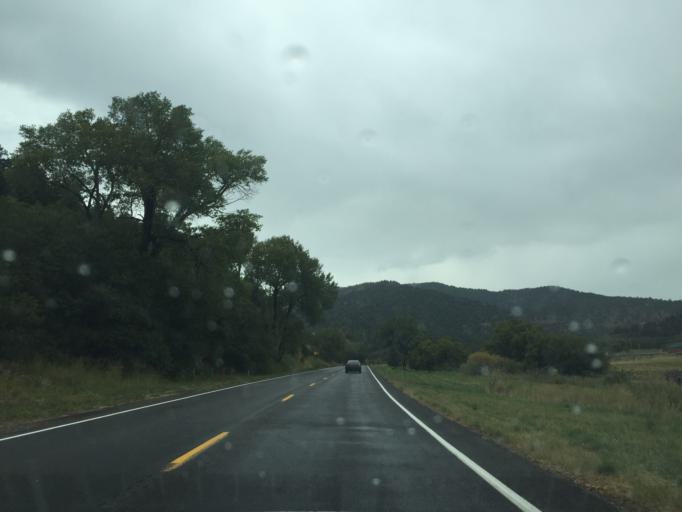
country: US
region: Utah
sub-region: Kane County
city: Kanab
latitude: 37.3356
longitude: -112.6033
